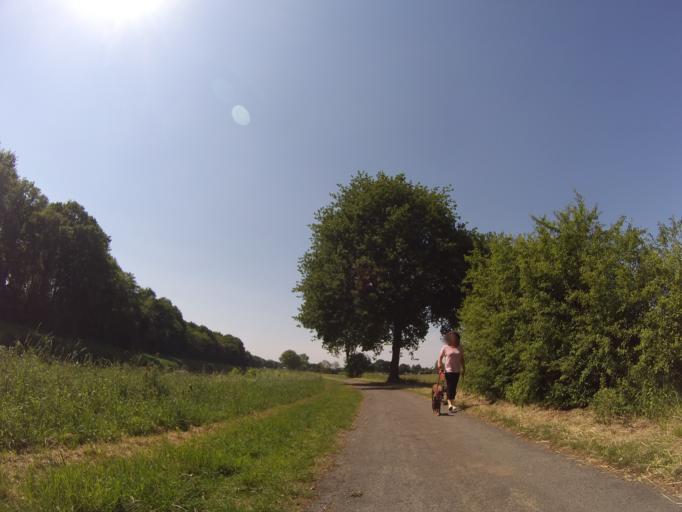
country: DE
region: Lower Saxony
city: Emlichheim
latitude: 52.6013
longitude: 6.8449
